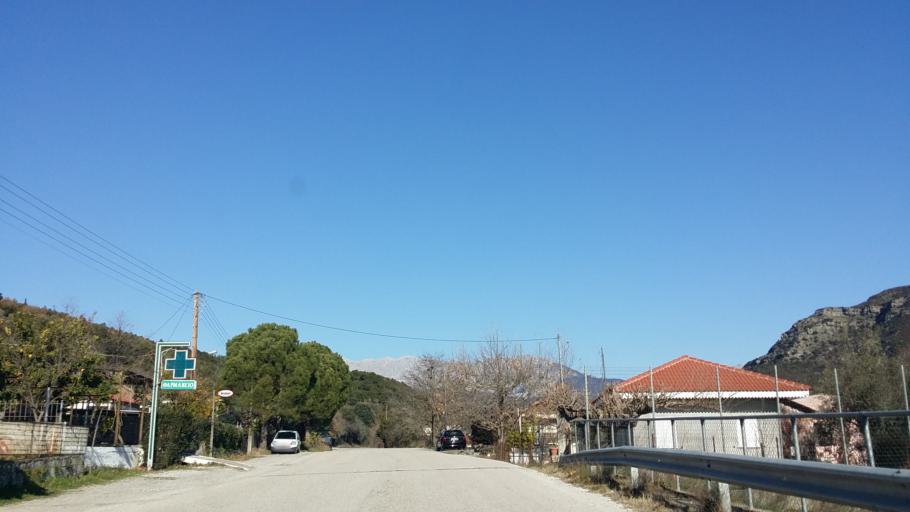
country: GR
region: West Greece
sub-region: Nomos Aitolias kai Akarnanias
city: Sardinia
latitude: 38.8934
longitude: 21.3478
